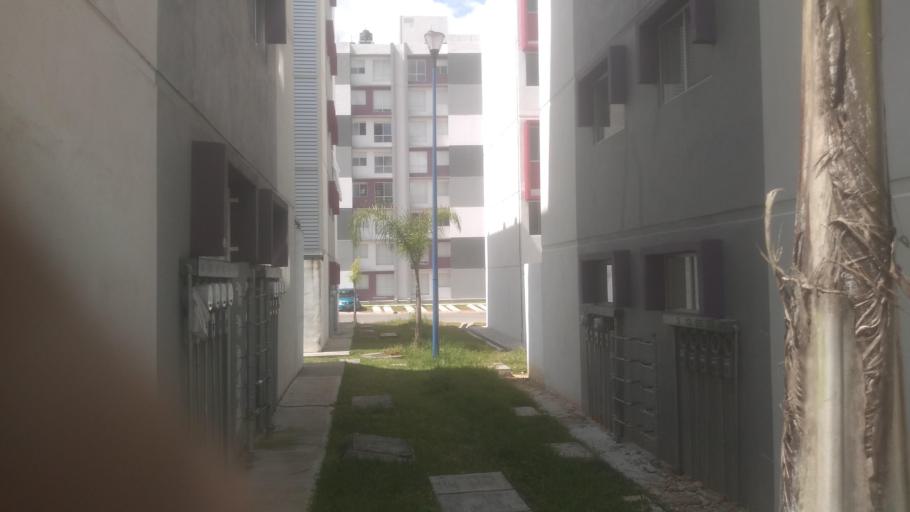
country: MX
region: Veracruz
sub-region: Ixtaczoquitlan
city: Buenavista
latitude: 18.8823
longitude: -97.0608
